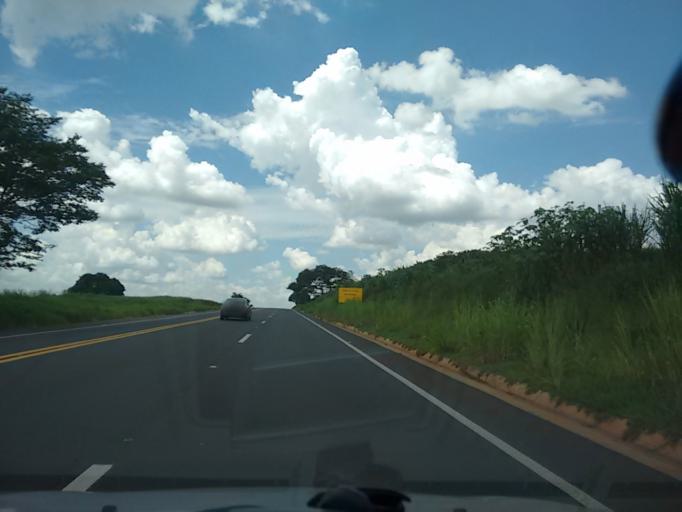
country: BR
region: Sao Paulo
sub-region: Osvaldo Cruz
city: Osvaldo Cruz
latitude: -21.8663
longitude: -50.8511
